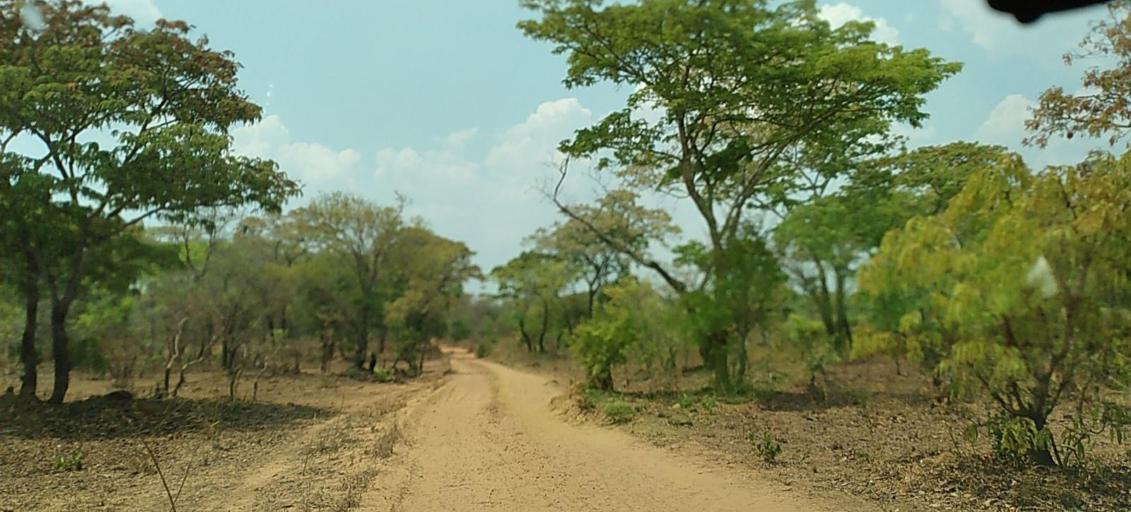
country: ZM
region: North-Western
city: Kabompo
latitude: -13.6419
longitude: 24.3807
